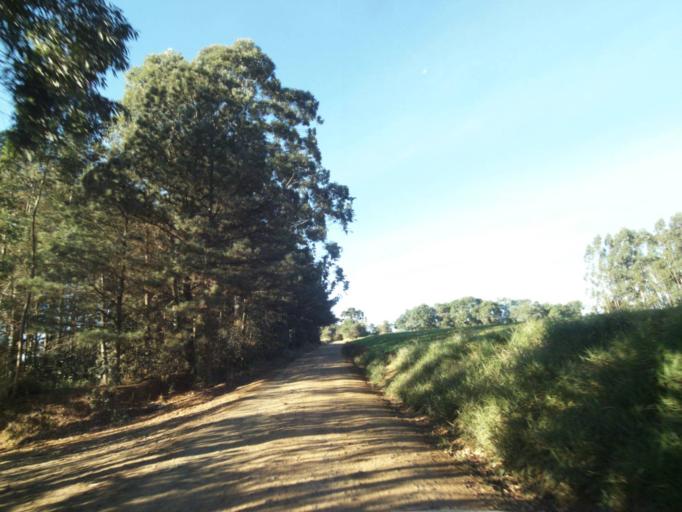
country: BR
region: Parana
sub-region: Tibagi
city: Tibagi
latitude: -24.5417
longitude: -50.6132
